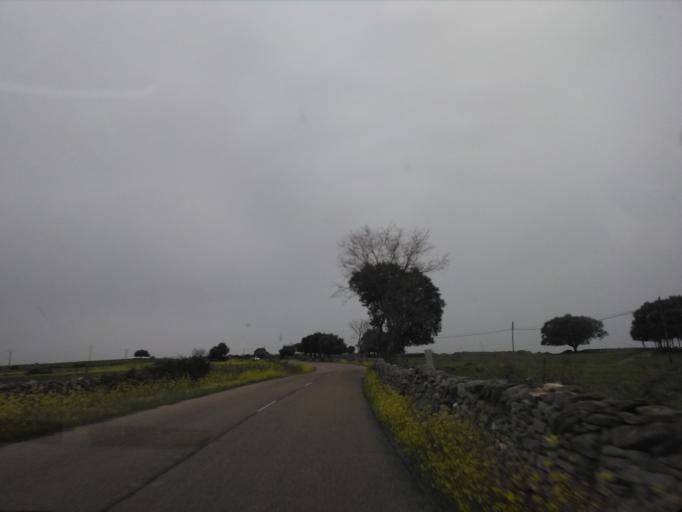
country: ES
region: Castille and Leon
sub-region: Provincia de Salamanca
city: Yecla de Yeltes
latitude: 40.9770
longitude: -6.4715
